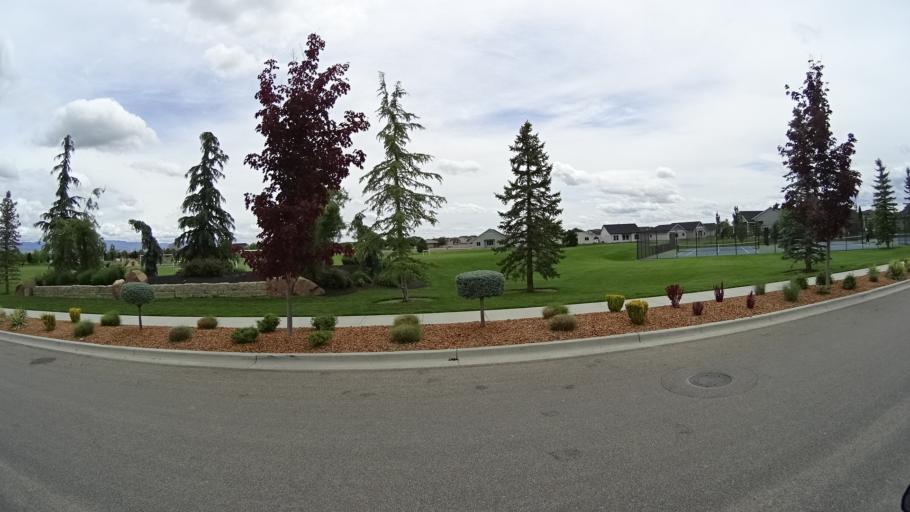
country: US
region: Idaho
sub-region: Ada County
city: Star
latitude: 43.7039
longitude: -116.4283
